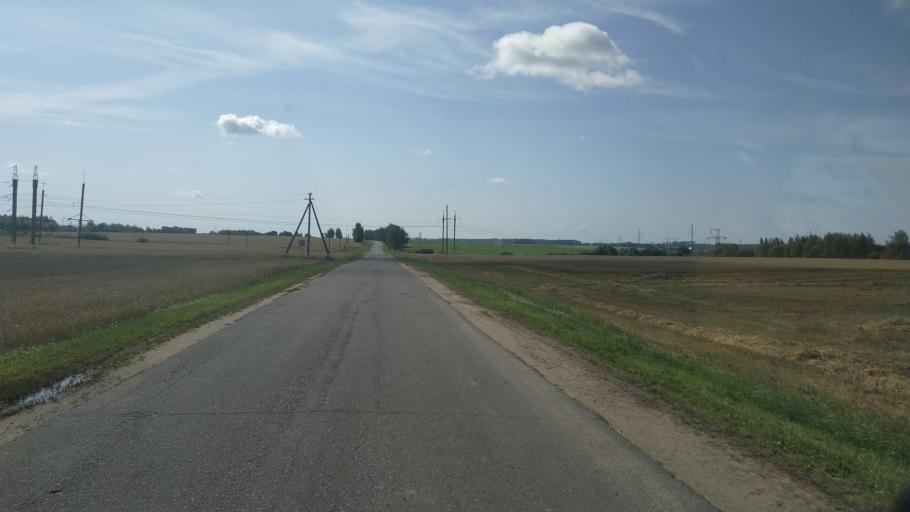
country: BY
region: Mogilev
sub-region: Mahilyowski Rayon
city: Veyno
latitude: 53.7915
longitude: 30.4310
